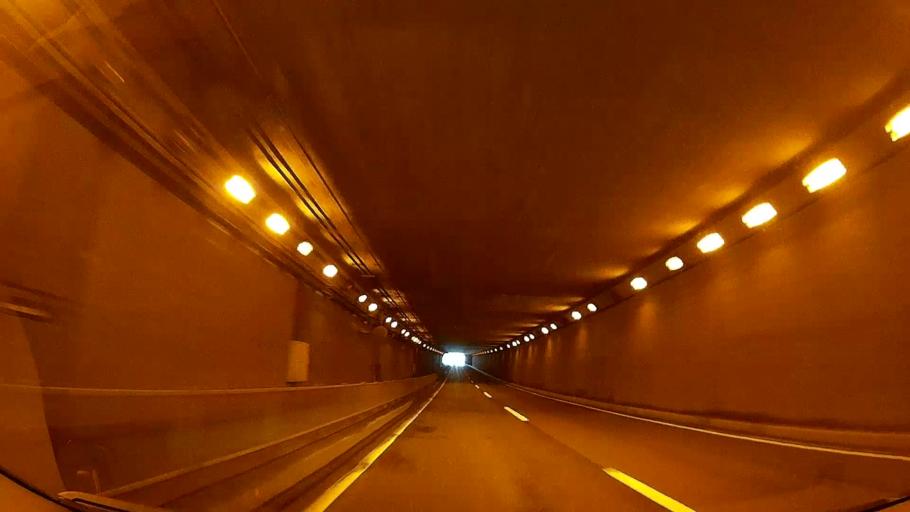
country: JP
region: Hokkaido
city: Chitose
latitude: 42.7917
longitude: 141.6768
